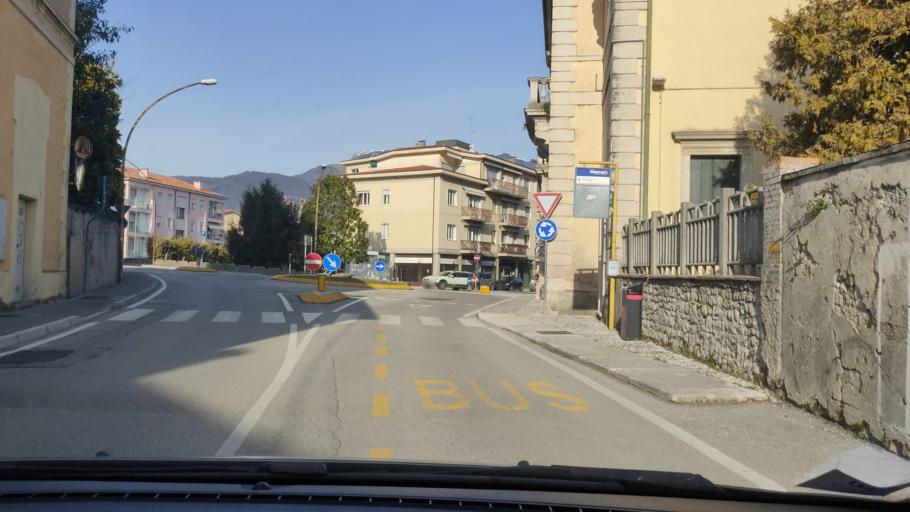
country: IT
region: Veneto
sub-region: Provincia di Treviso
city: Vittorio Veneto
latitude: 45.9785
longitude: 12.2958
